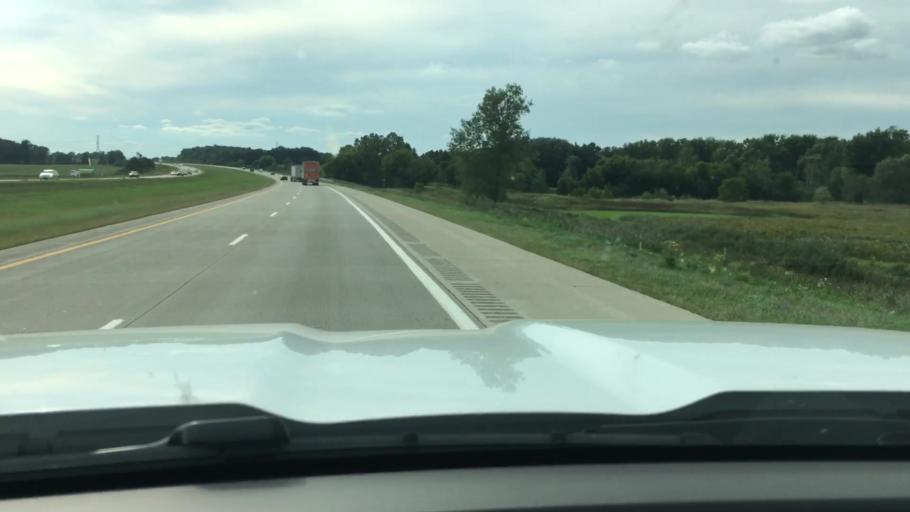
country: US
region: Michigan
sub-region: Genesee County
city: Davison
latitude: 43.0164
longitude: -83.4657
